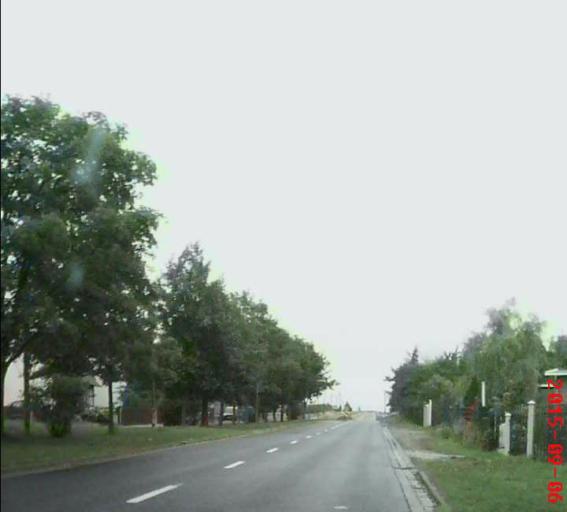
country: DE
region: Thuringia
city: Sollstedt
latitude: 51.2904
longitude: 10.4454
